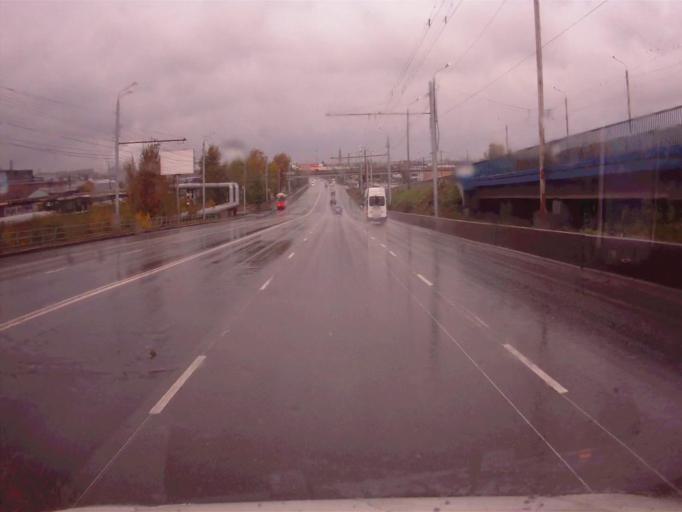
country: RU
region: Chelyabinsk
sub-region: Gorod Chelyabinsk
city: Chelyabinsk
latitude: 55.1985
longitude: 61.3859
